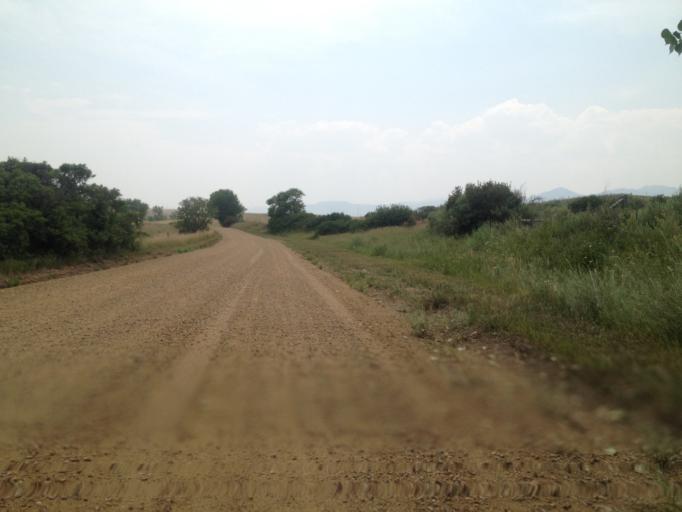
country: US
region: Colorado
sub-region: Boulder County
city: Superior
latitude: 39.9506
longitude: -105.1837
